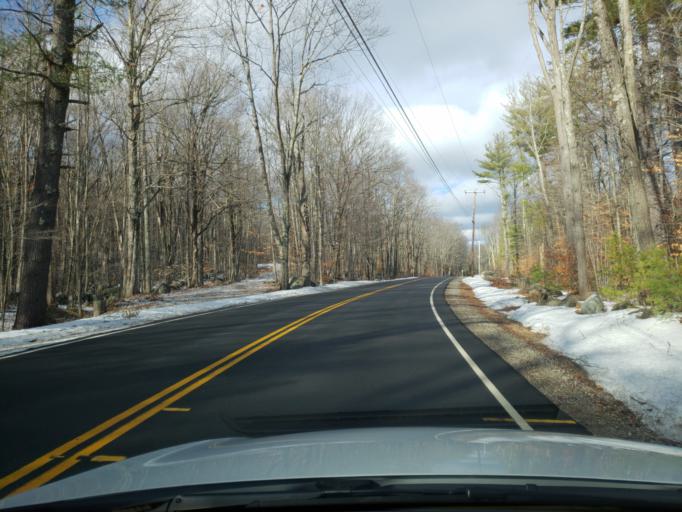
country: US
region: New Hampshire
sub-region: Hillsborough County
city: Greenfield
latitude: 43.0029
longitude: -71.8326
